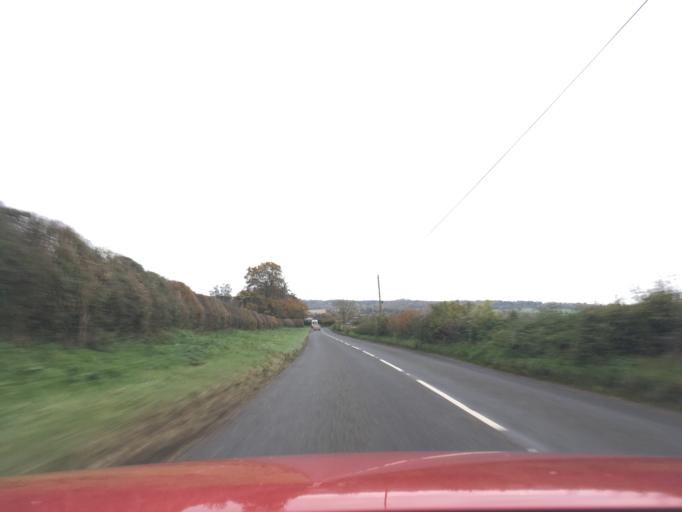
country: GB
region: England
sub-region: Dorset
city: Sherborne
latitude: 50.9572
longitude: -2.5385
